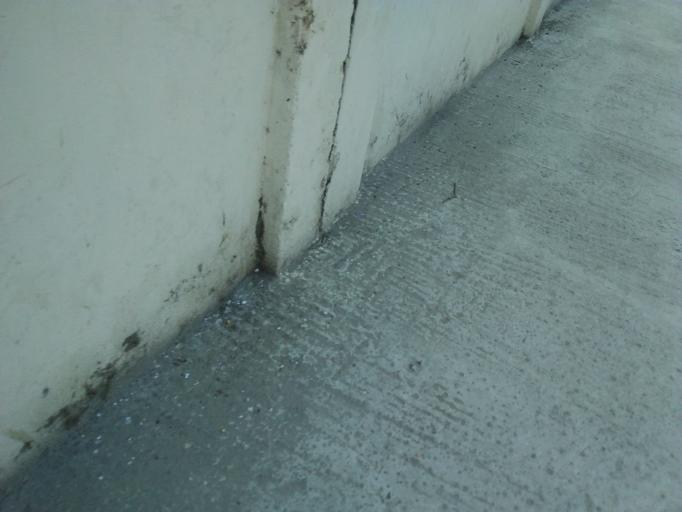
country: BD
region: Khulna
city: Khulna
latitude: 22.8049
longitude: 89.5780
